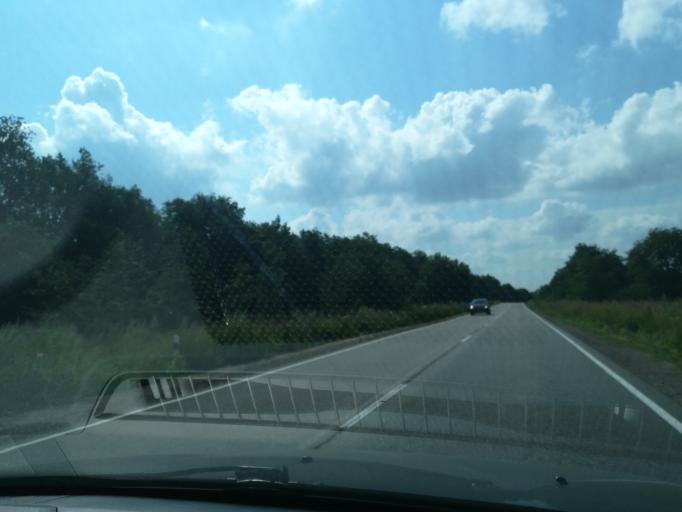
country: RU
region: Leningrad
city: Kopor'ye
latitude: 59.6930
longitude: 29.0547
